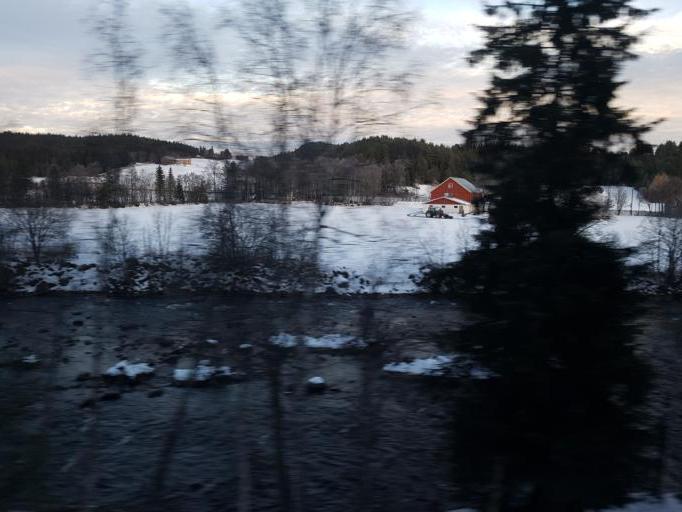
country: NO
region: Sor-Trondelag
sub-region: Rennebu
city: Berkak
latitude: 62.8724
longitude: 10.0638
